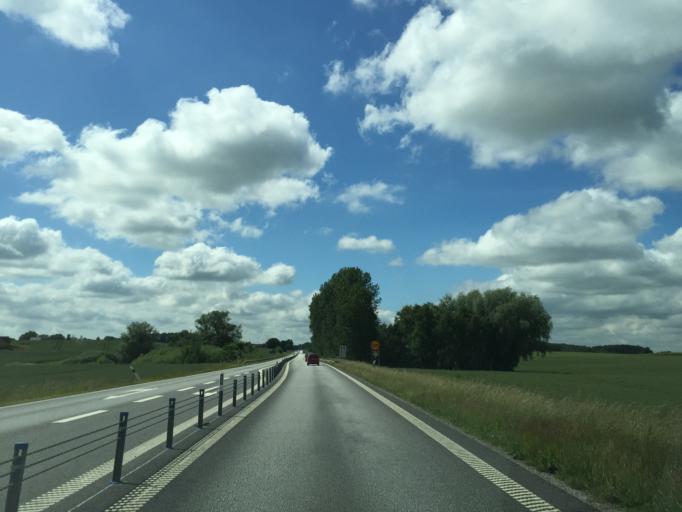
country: SE
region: Skane
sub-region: Skurups Kommun
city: Skurup
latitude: 55.4926
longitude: 13.5253
